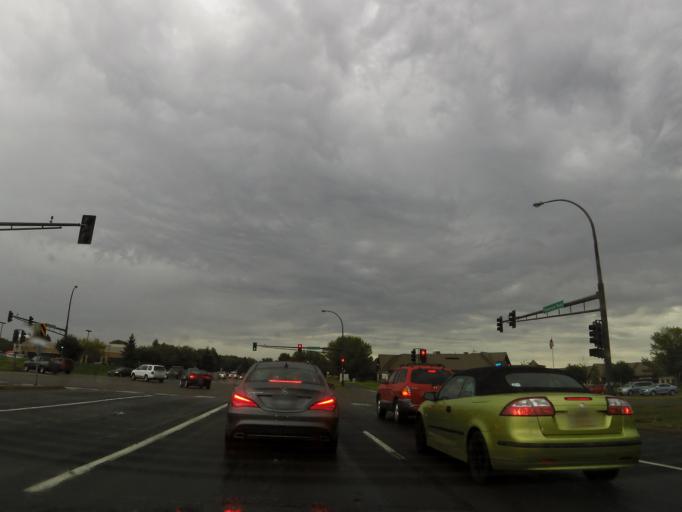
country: US
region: Minnesota
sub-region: Washington County
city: Woodbury
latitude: 44.9378
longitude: -92.9345
